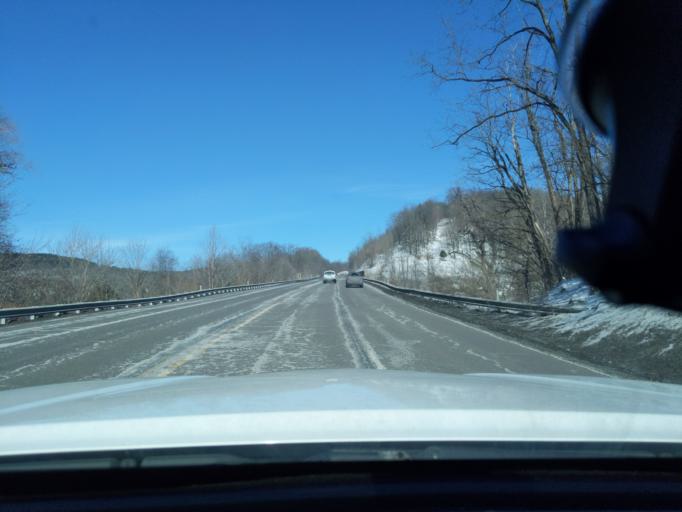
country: US
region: Maryland
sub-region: Allegany County
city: Westernport
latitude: 39.5257
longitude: -79.0170
